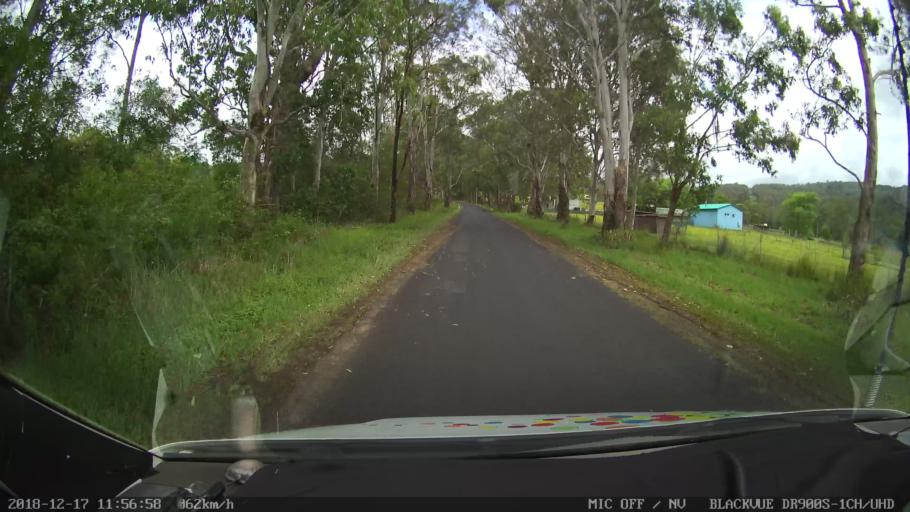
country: AU
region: New South Wales
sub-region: Kyogle
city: Kyogle
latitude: -28.5432
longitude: 152.5771
